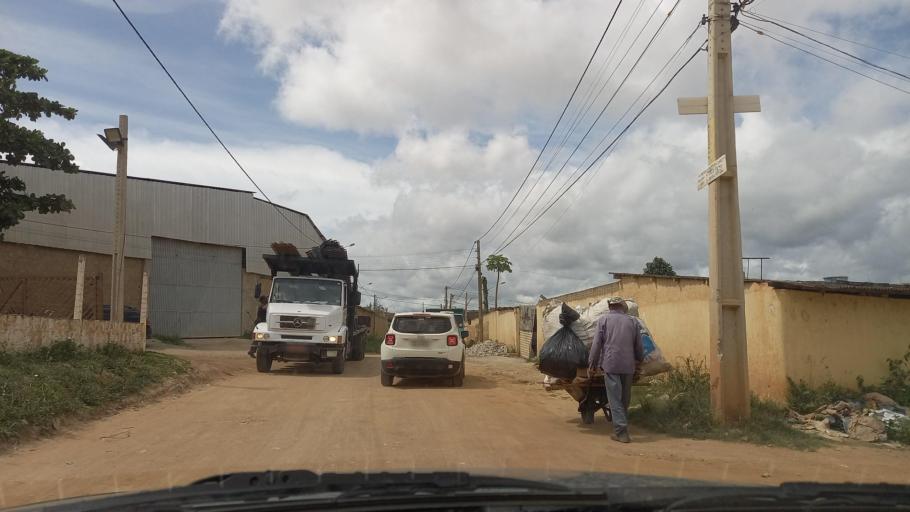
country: BR
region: Pernambuco
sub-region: Gravata
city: Gravata
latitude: -8.1864
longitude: -35.5819
